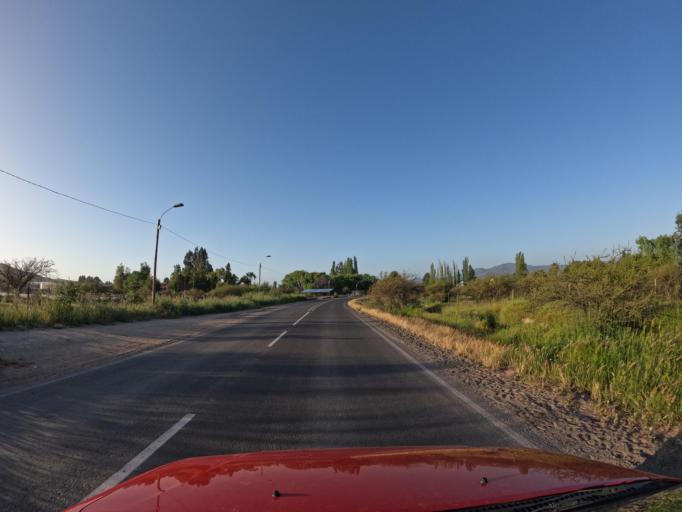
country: CL
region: O'Higgins
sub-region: Provincia de Cachapoal
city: San Vicente
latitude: -34.3142
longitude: -71.3853
